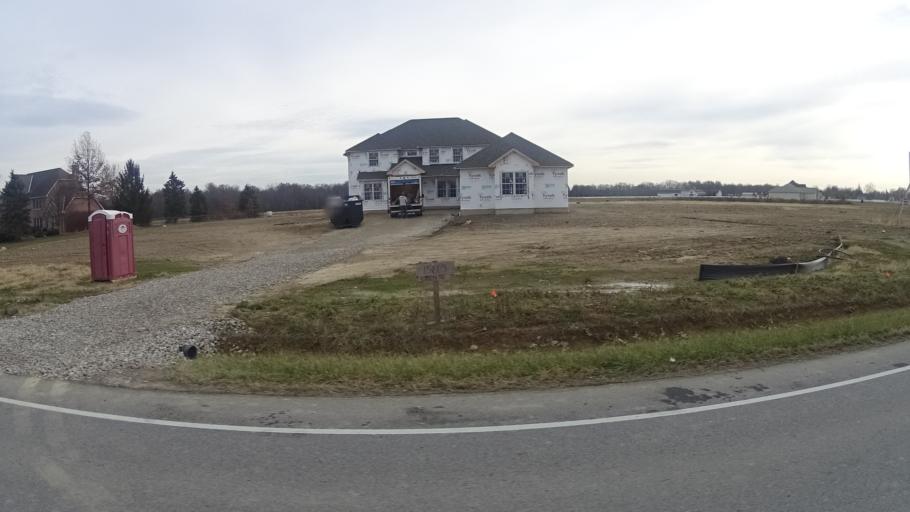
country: US
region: Ohio
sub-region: Lorain County
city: Eaton Estates
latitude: 41.3022
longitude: -81.9532
